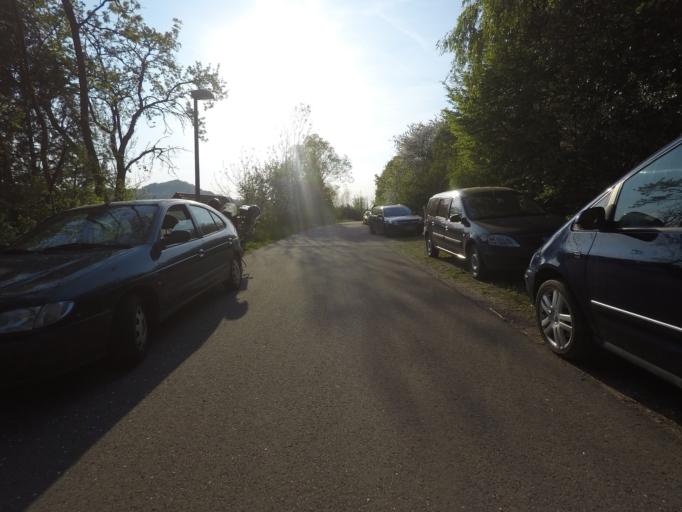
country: DE
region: Baden-Wuerttemberg
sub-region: Tuebingen Region
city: Eningen unter Achalm
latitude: 48.4788
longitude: 9.2429
